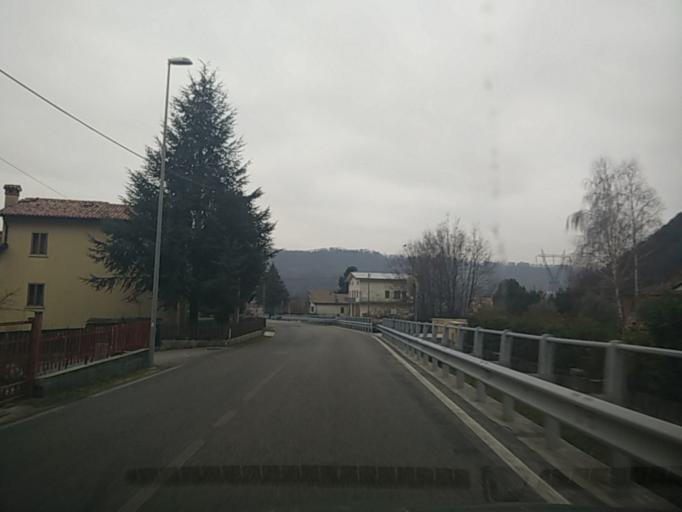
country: IT
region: Veneto
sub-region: Provincia di Treviso
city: Cison di Valmarino
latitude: 45.9773
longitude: 12.1748
